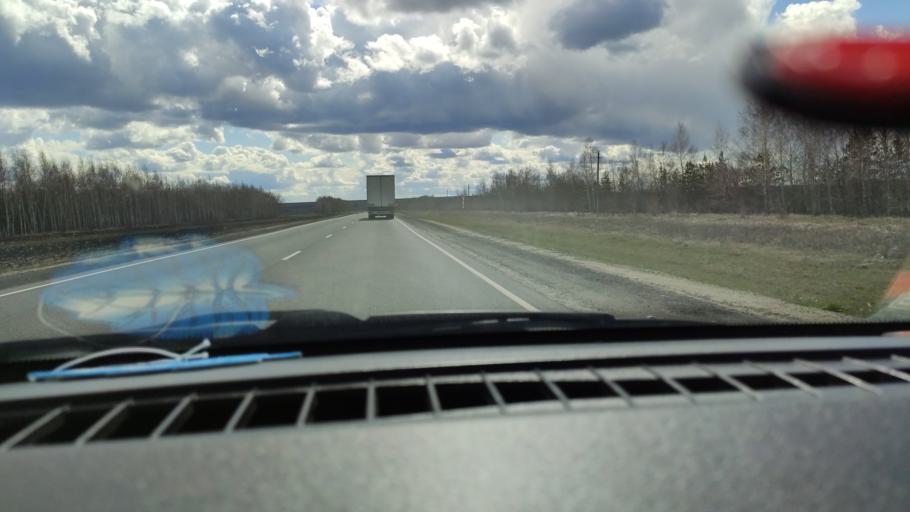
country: RU
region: Samara
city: Syzran'
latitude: 52.9854
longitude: 48.3169
